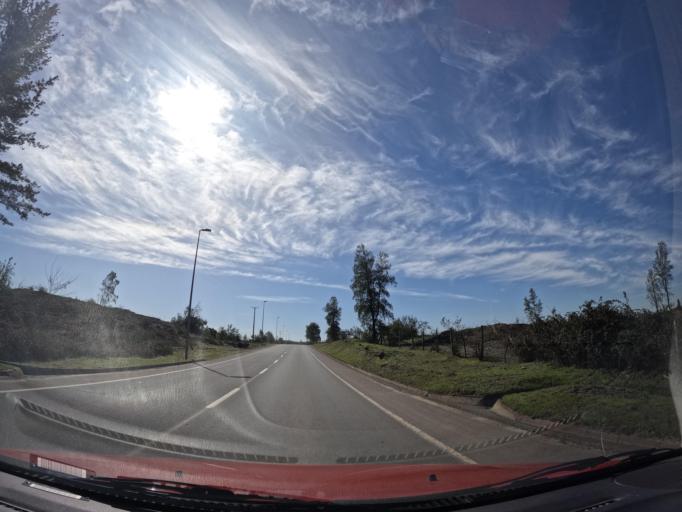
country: CL
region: Biobio
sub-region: Provincia de Biobio
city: Cabrero
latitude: -36.9373
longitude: -72.3452
